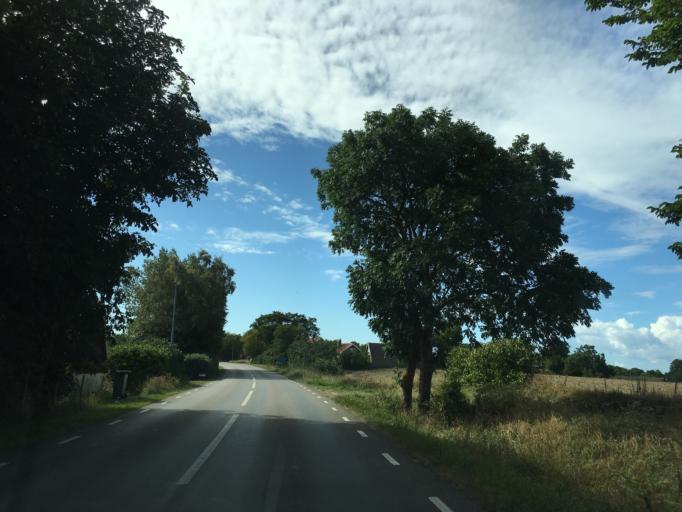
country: SE
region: Kalmar
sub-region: Morbylanga Kommun
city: Moerbylanga
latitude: 56.4462
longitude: 16.4269
